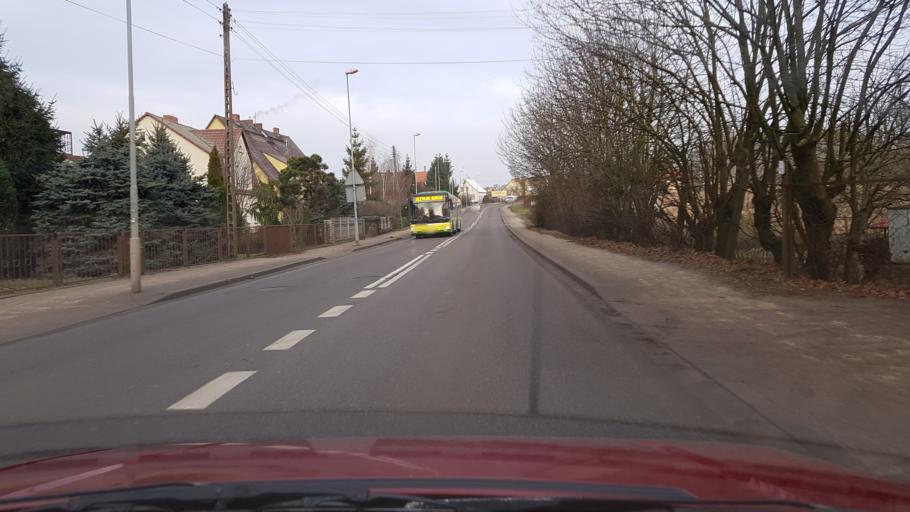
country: PL
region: West Pomeranian Voivodeship
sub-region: Powiat policki
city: Police
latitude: 53.5401
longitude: 14.5764
